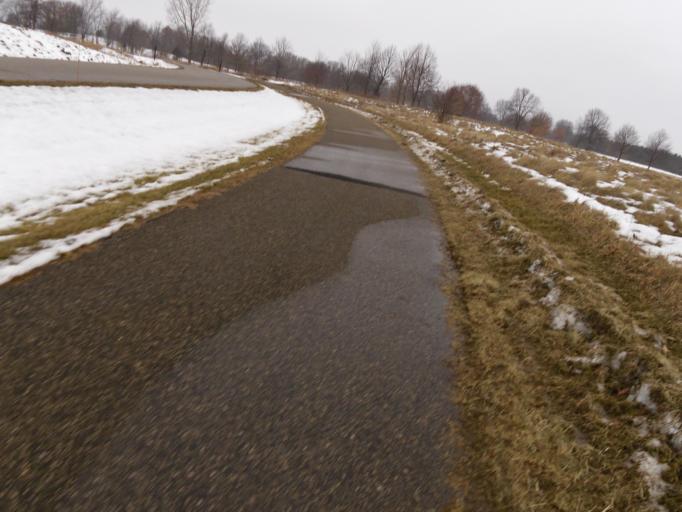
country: US
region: Minnesota
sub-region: Washington County
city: Lake Elmo
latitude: 44.9888
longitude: -92.8894
